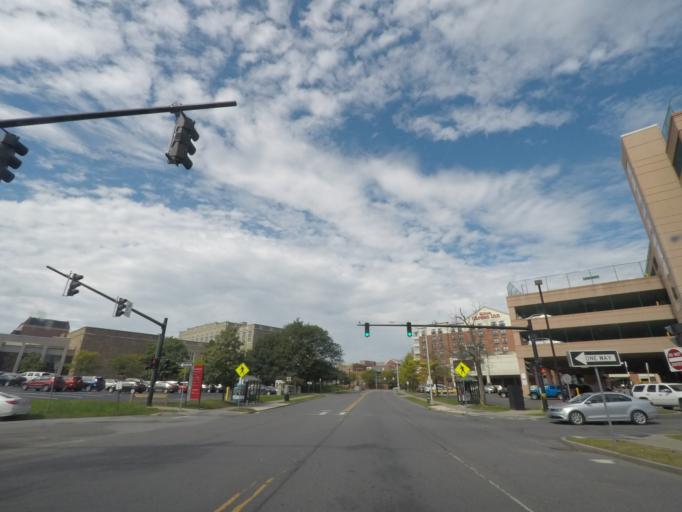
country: US
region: New York
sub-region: Albany County
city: Albany
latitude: 42.6510
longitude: -73.7759
